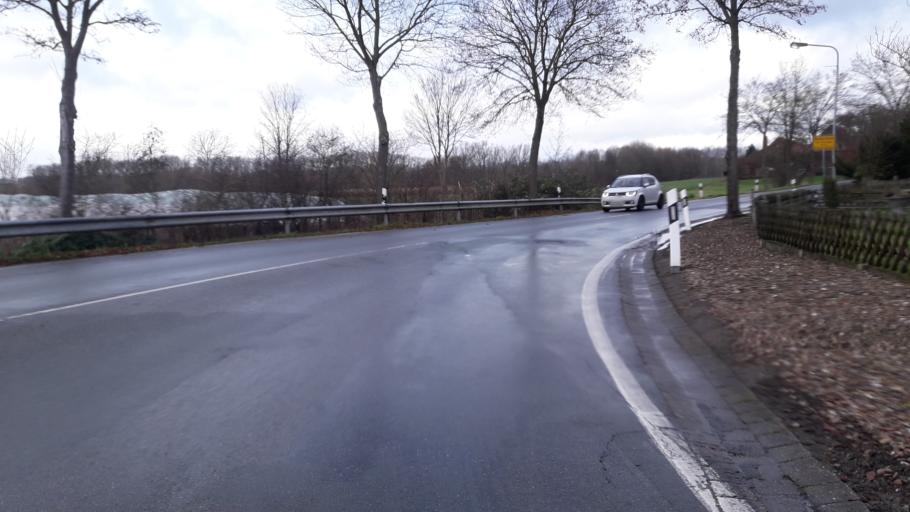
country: DE
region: North Rhine-Westphalia
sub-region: Regierungsbezirk Detmold
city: Petershagen
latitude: 52.3331
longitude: 8.9530
